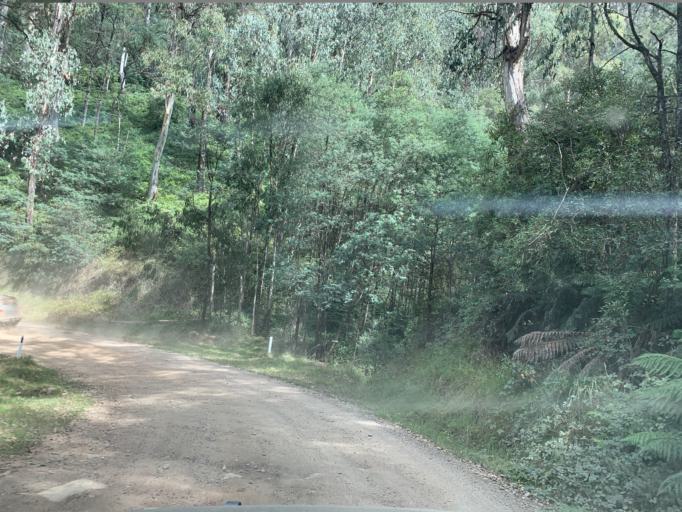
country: AU
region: Victoria
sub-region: Mansfield
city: Mansfield
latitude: -37.1024
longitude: 146.4977
